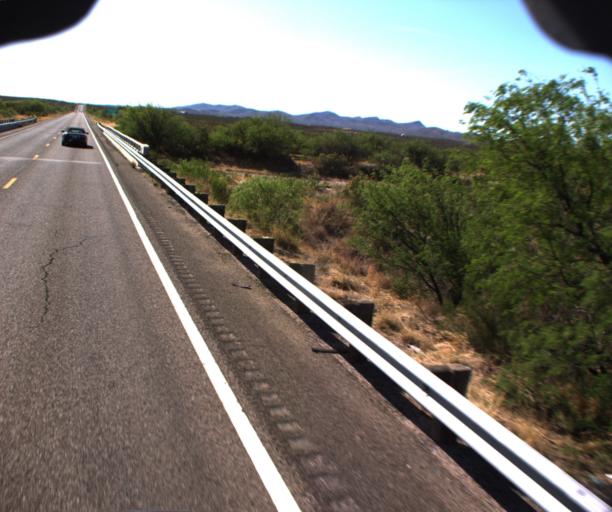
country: US
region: Arizona
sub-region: Cochise County
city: Tombstone
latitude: 31.7602
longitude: -110.1113
